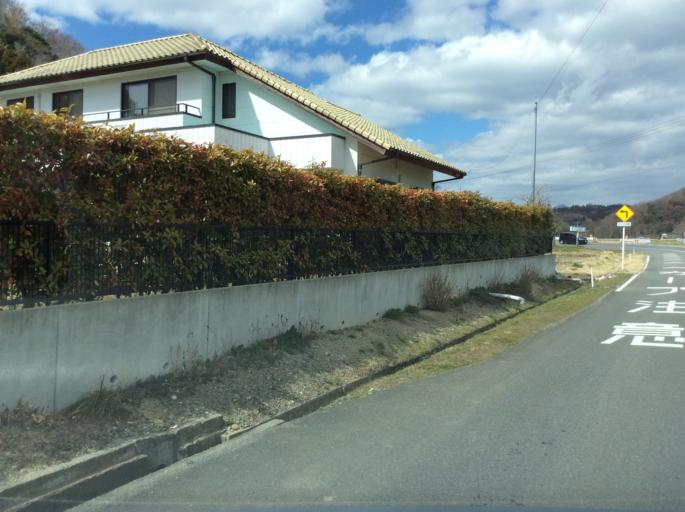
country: JP
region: Fukushima
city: Iwaki
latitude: 37.0872
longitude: 140.9447
